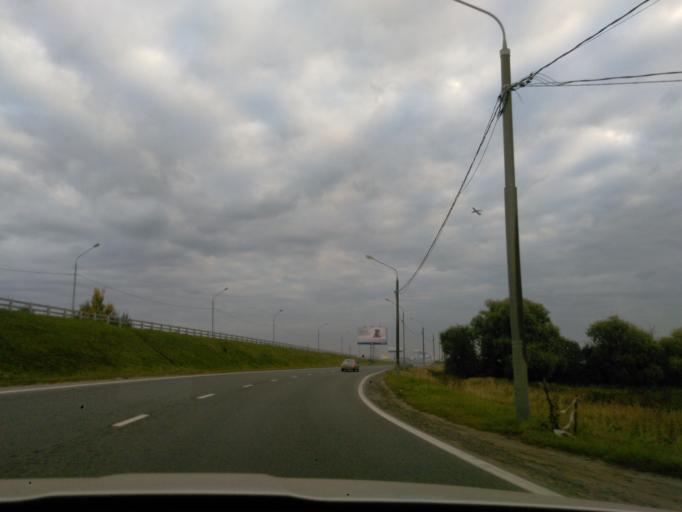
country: RU
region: Moskovskaya
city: Novopodrezkovo
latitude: 55.9549
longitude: 37.3464
